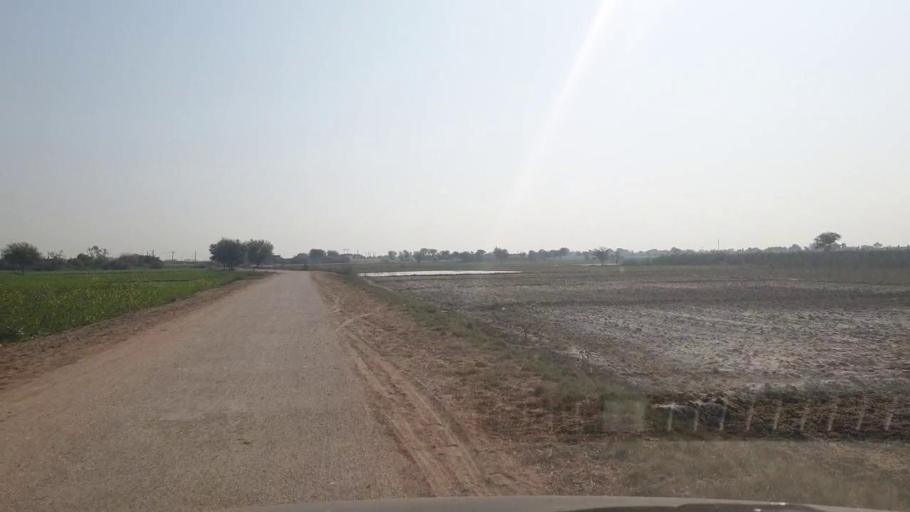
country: PK
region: Sindh
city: Tando Adam
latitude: 25.7462
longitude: 68.6136
